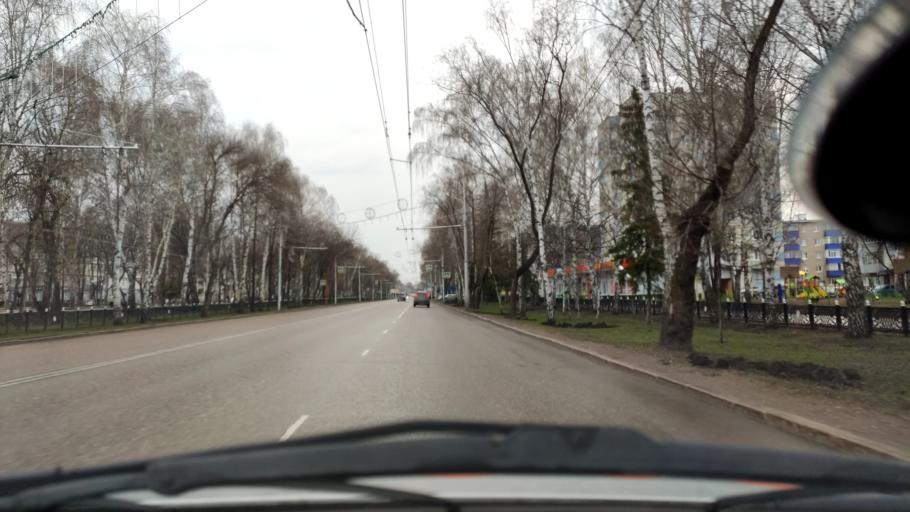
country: RU
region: Bashkortostan
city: Sterlitamak
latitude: 53.6330
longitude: 55.9334
